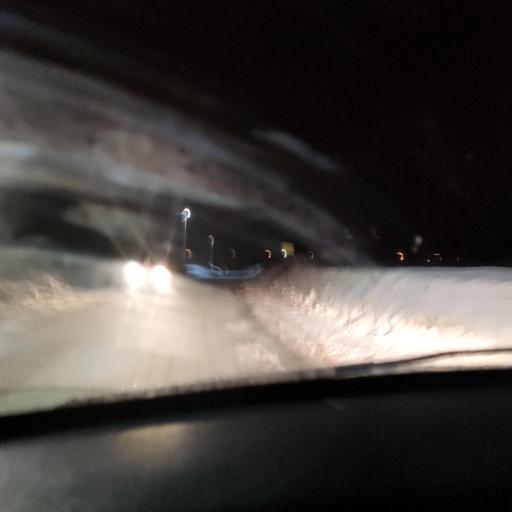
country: RU
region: Perm
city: Polazna
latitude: 58.1792
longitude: 56.4050
